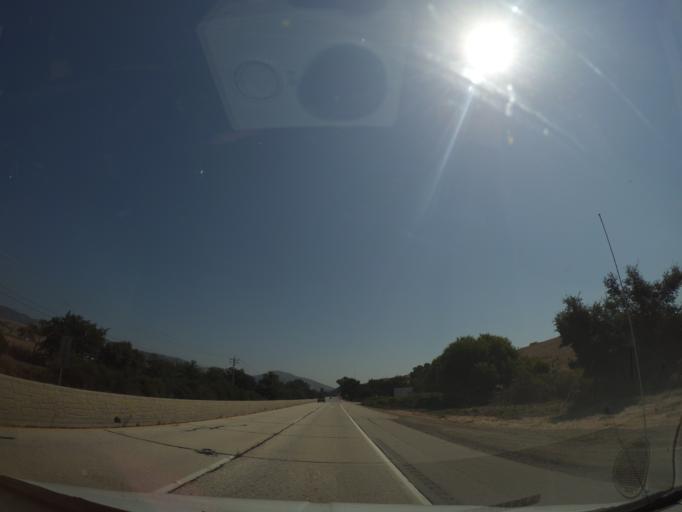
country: US
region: California
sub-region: San Luis Obispo County
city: San Luis Obispo
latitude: 35.3105
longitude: -120.6840
